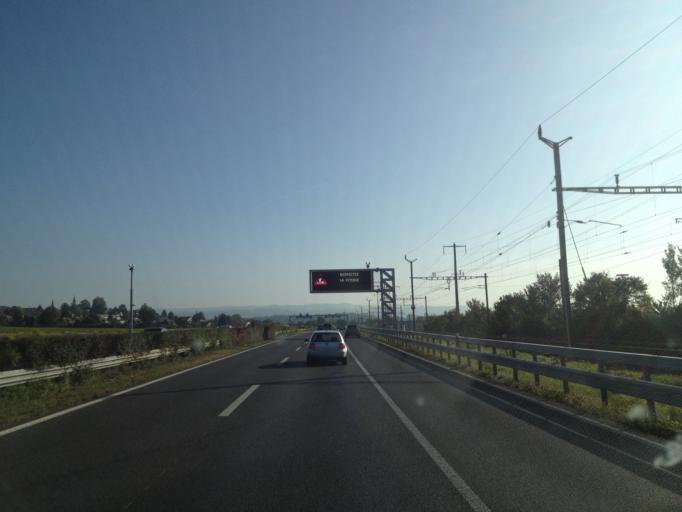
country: CH
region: Vaud
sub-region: Morges District
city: Preverenges
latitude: 46.5272
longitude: 6.5323
